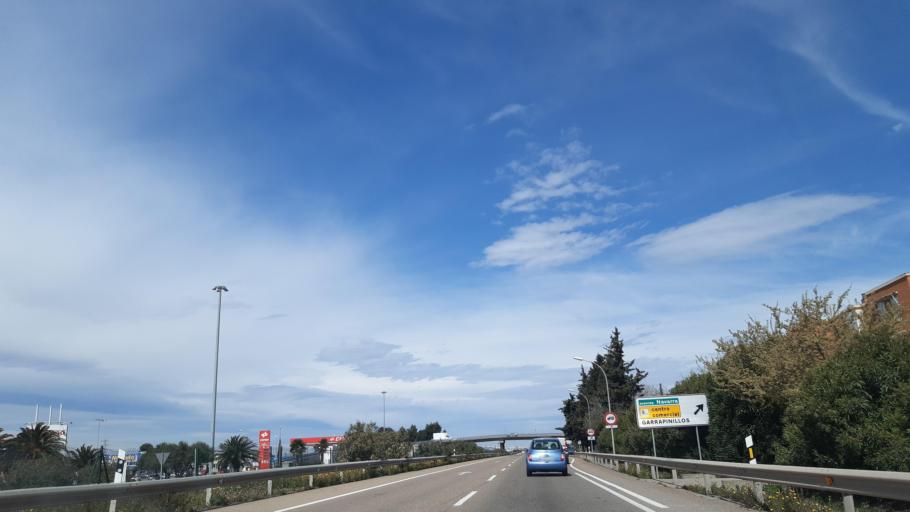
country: ES
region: Aragon
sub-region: Provincia de Zaragoza
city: Utebo
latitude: 41.7031
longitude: -1.0022
